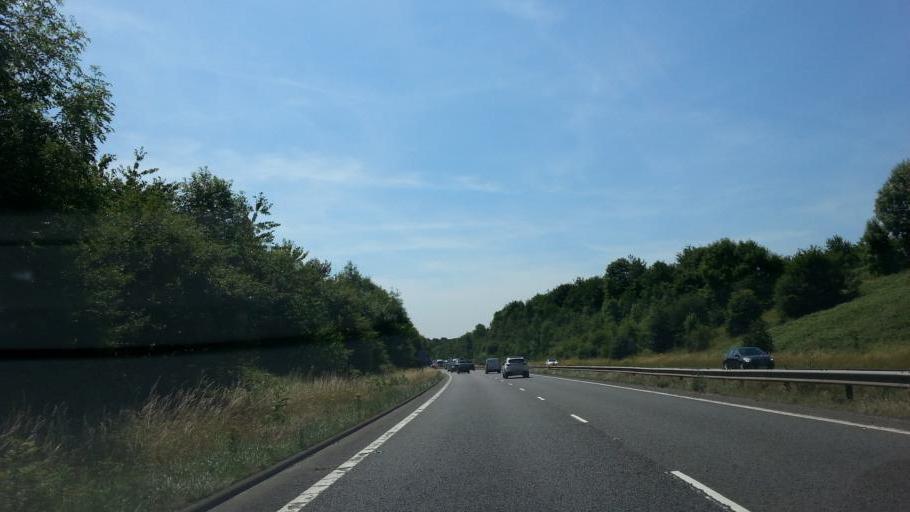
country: GB
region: England
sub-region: Derbyshire
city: Heage
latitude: 53.0299
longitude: -1.4419
